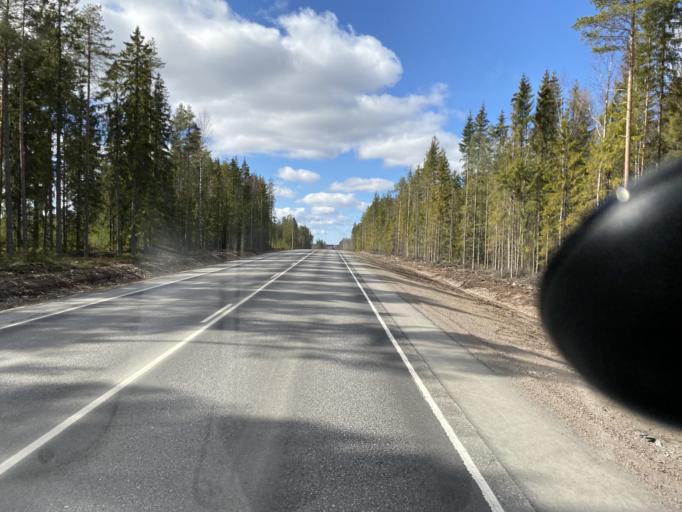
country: FI
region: Satakunta
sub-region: Rauma
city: Koeylioe
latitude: 61.1641
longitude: 22.3483
